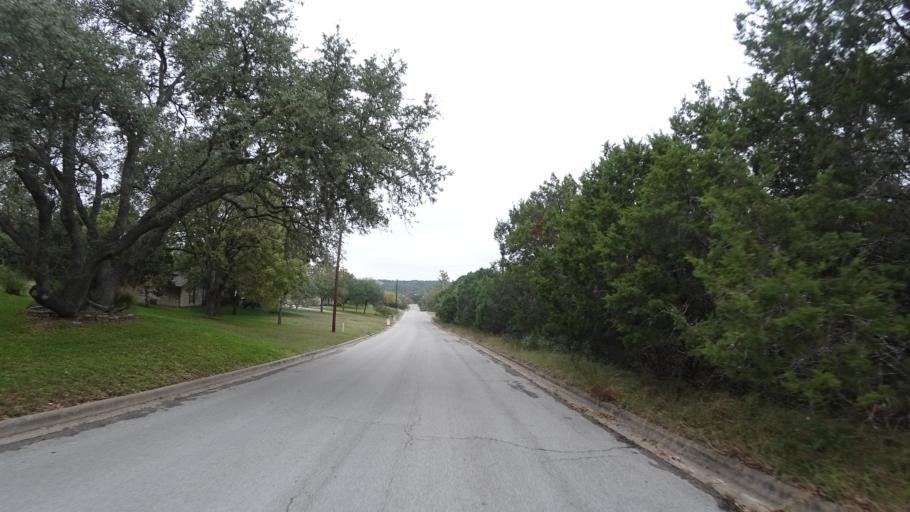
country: US
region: Texas
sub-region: Travis County
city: Barton Creek
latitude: 30.2233
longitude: -97.9067
